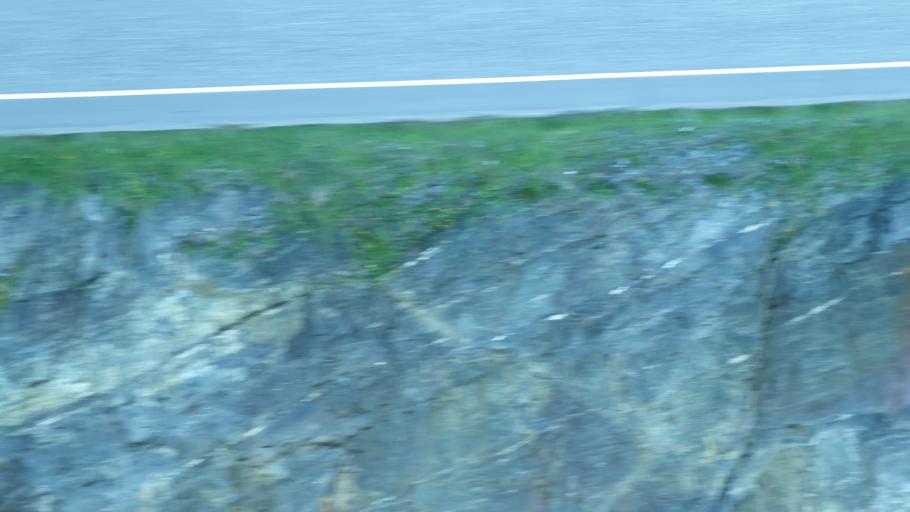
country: NO
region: Sor-Trondelag
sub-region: Rissa
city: Rissa
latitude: 63.5052
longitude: 10.1306
